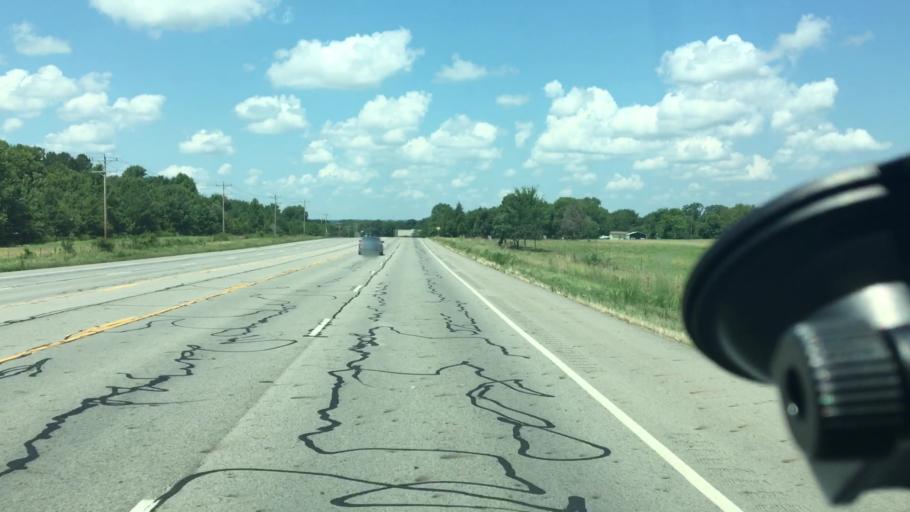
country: US
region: Arkansas
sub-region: Sebastian County
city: Barling
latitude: 35.3199
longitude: -94.2438
